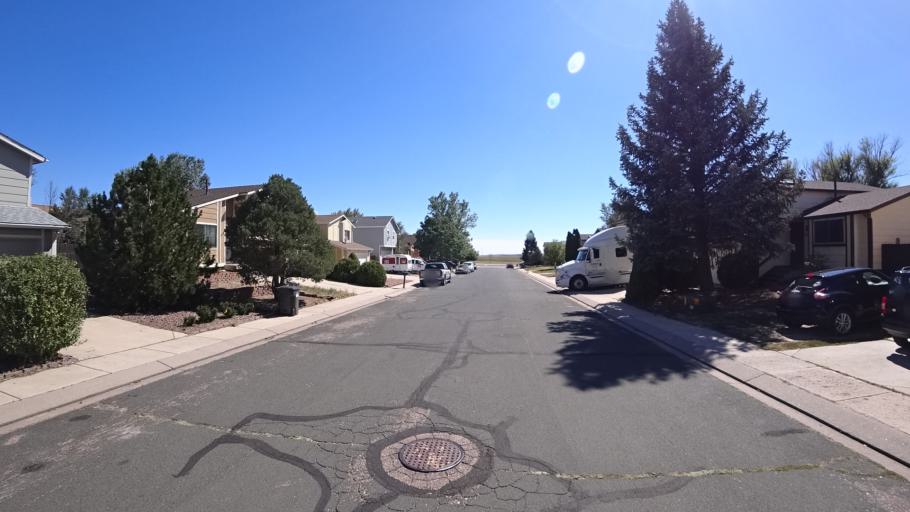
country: US
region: Colorado
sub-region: El Paso County
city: Stratmoor
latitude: 38.7829
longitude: -104.7419
